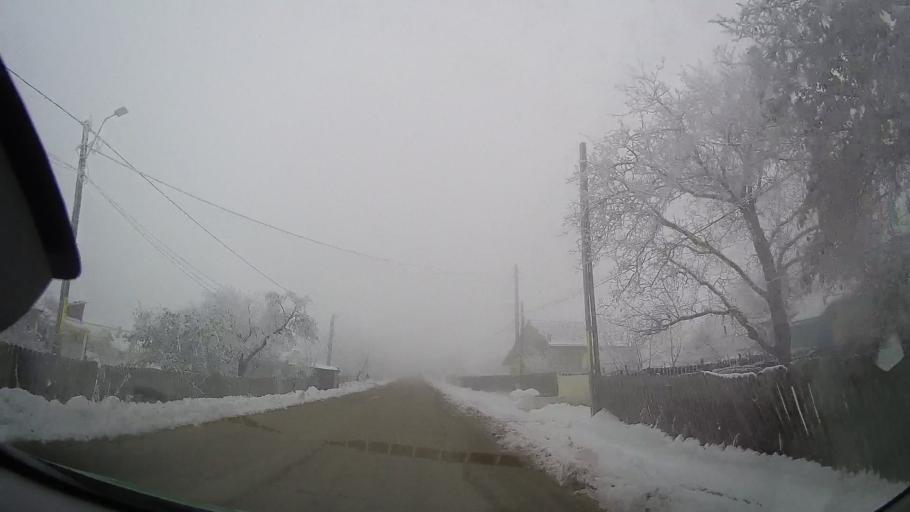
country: RO
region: Iasi
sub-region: Comuna Tansa
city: Suhulet
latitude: 46.8991
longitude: 27.2620
